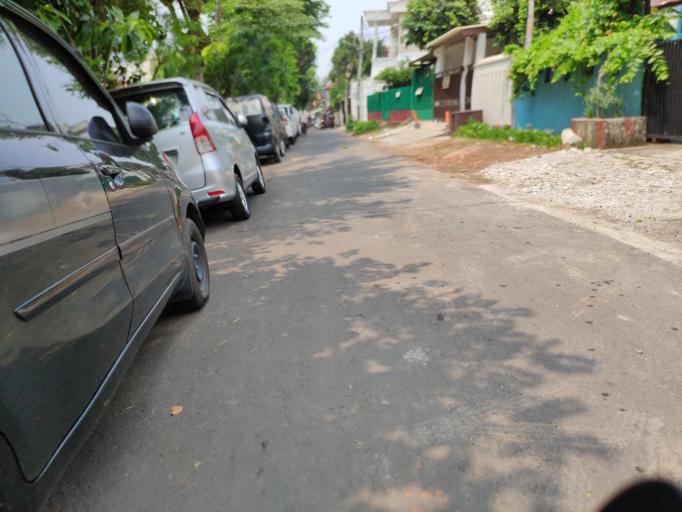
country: ID
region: Jakarta Raya
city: Jakarta
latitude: -6.2081
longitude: 106.8608
